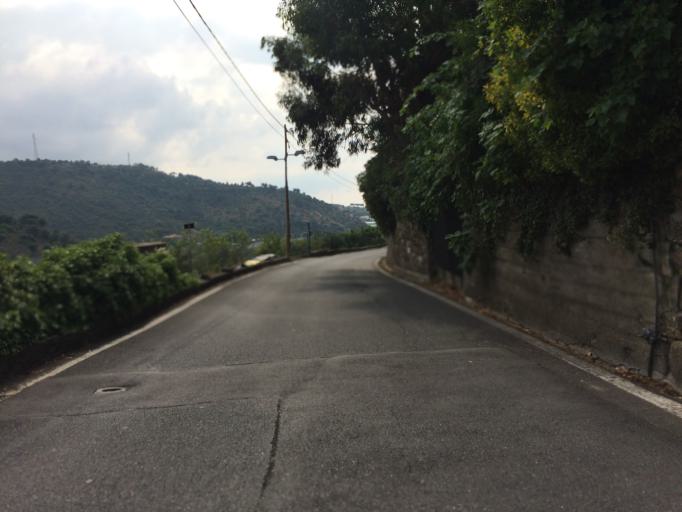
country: IT
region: Liguria
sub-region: Provincia di Imperia
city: San Remo
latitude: 43.8375
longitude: 7.7557
